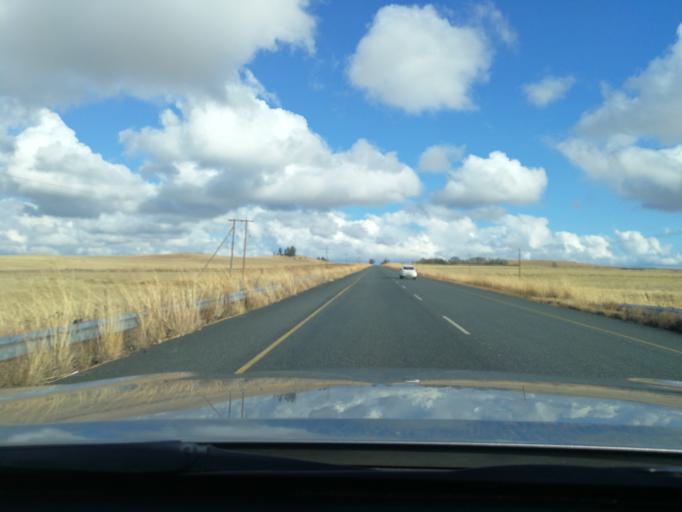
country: ZA
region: Orange Free State
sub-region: Thabo Mofutsanyana District Municipality
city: Reitz
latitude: -27.9898
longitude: 28.3749
